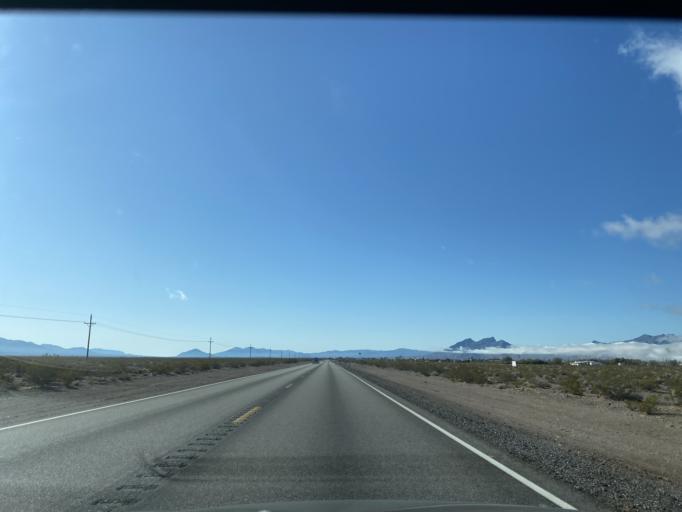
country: US
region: Nevada
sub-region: Nye County
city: Beatty
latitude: 36.5198
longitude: -116.4197
